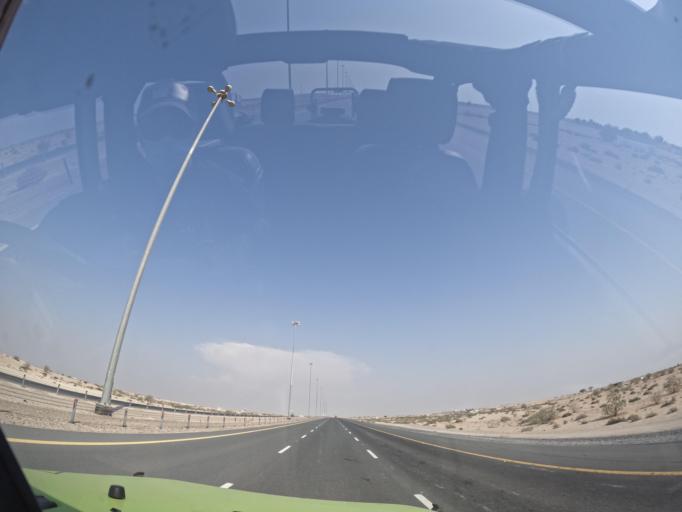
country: AE
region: Dubai
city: Dubai
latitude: 24.6761
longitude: 54.8379
